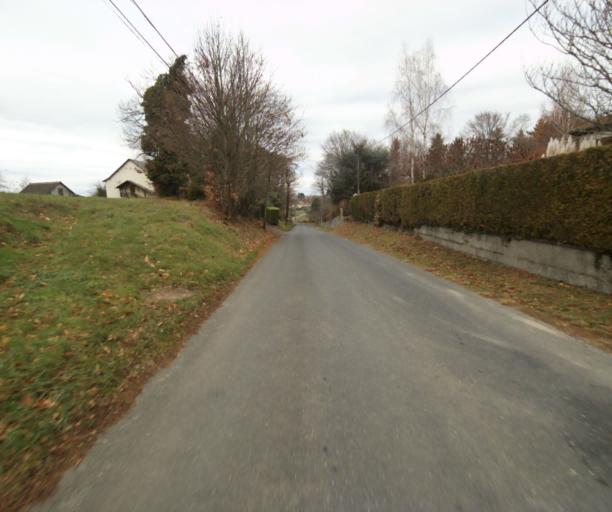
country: FR
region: Limousin
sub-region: Departement de la Correze
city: Sainte-Fortunade
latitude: 45.2275
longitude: 1.7643
